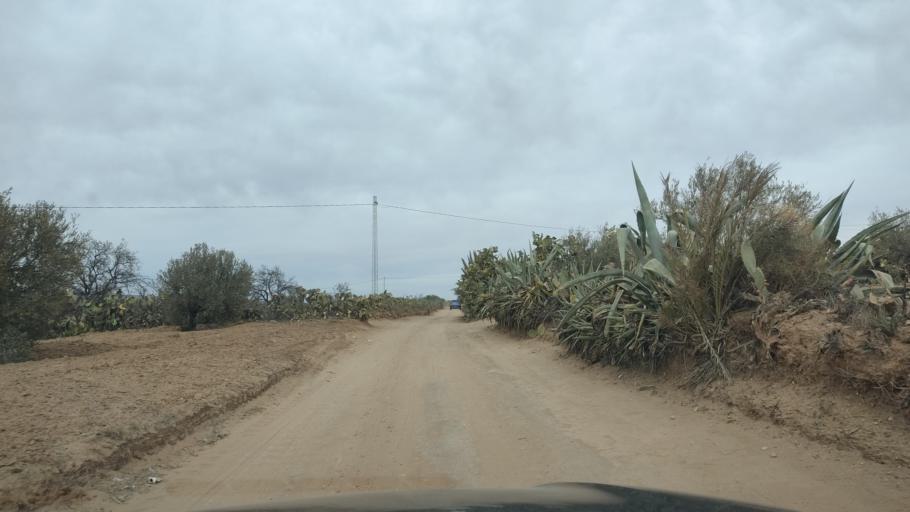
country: TN
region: Al Qasrayn
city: Kasserine
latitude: 35.2463
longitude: 8.9192
